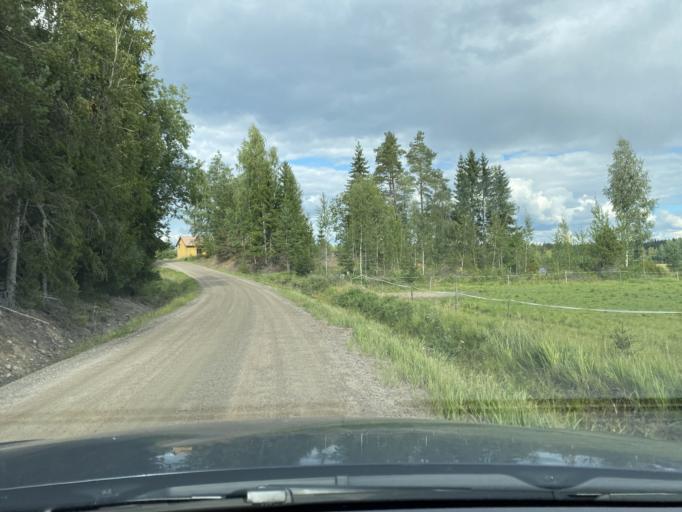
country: FI
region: Haeme
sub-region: Forssa
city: Humppila
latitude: 61.0687
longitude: 23.2701
